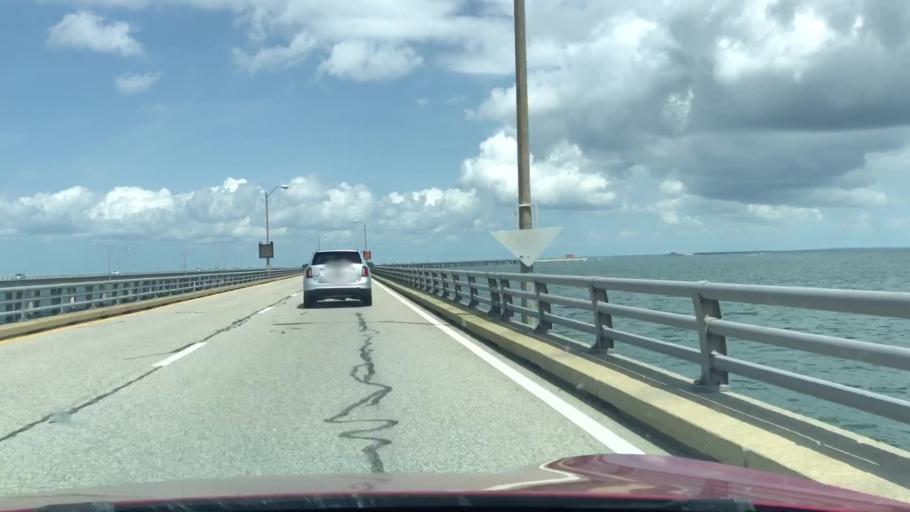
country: US
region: Virginia
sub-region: City of Virginia Beach
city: Virginia Beach
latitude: 37.0191
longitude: -76.0908
